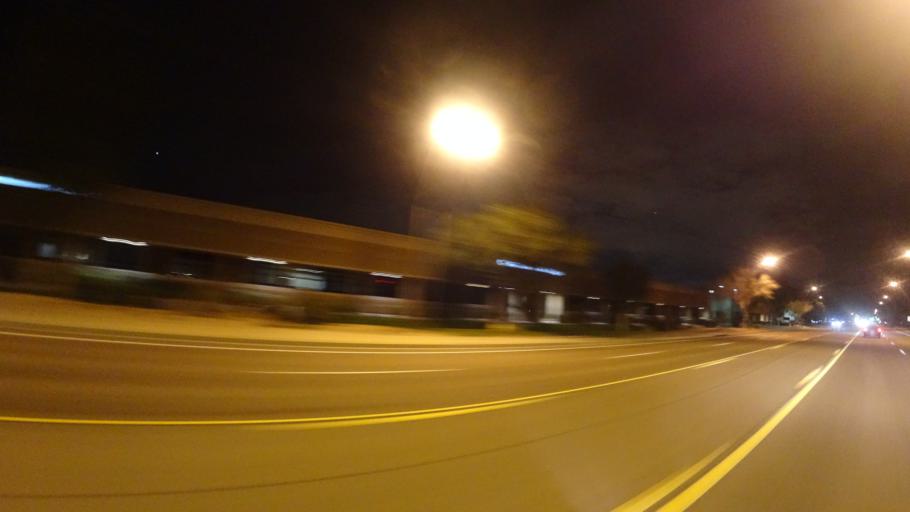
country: US
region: Arizona
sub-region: Maricopa County
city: Guadalupe
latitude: 33.3288
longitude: -111.9456
